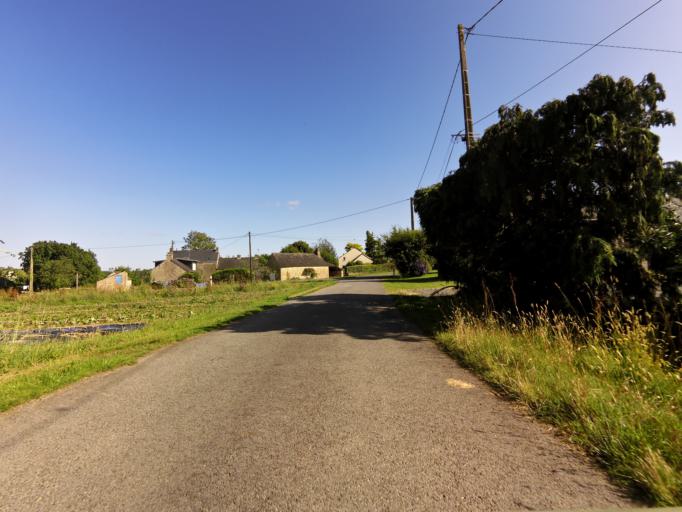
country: FR
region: Brittany
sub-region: Departement du Morbihan
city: Caden
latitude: 47.6337
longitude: -2.2617
